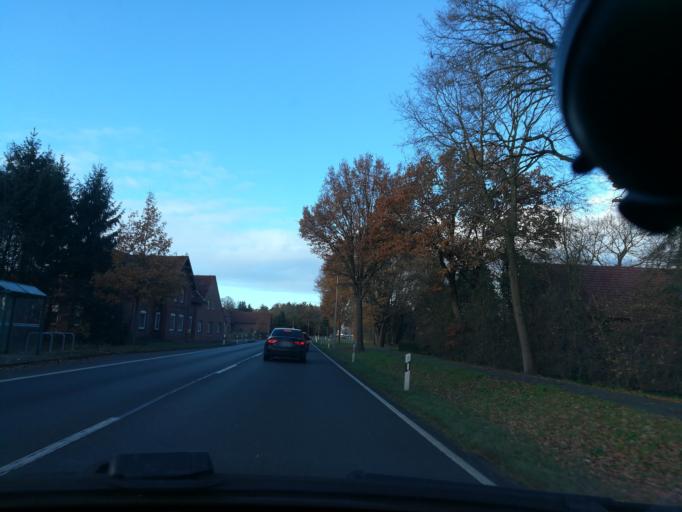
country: DE
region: Lower Saxony
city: Uchte
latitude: 52.4670
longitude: 8.9081
